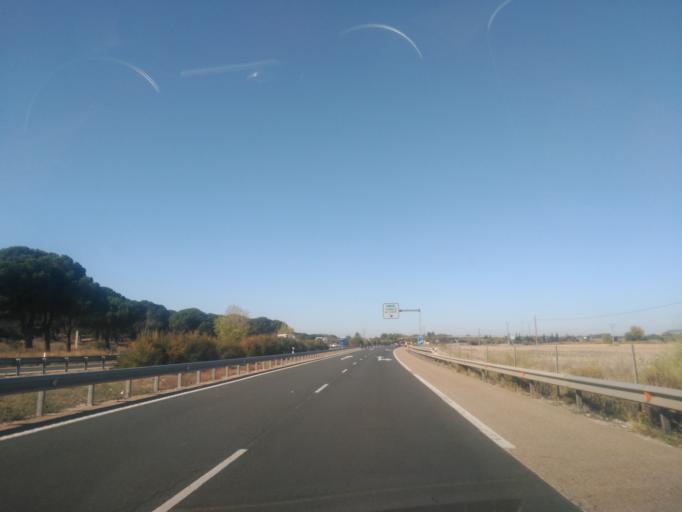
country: ES
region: Castille and Leon
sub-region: Provincia de Valladolid
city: Tudela de Duero
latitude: 41.5876
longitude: -4.5475
